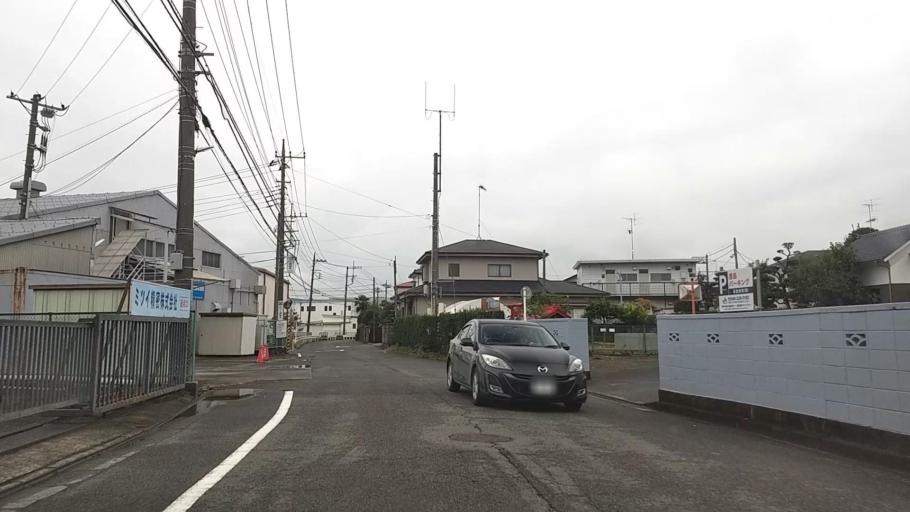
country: JP
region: Kanagawa
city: Atsugi
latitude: 35.4186
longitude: 139.3484
